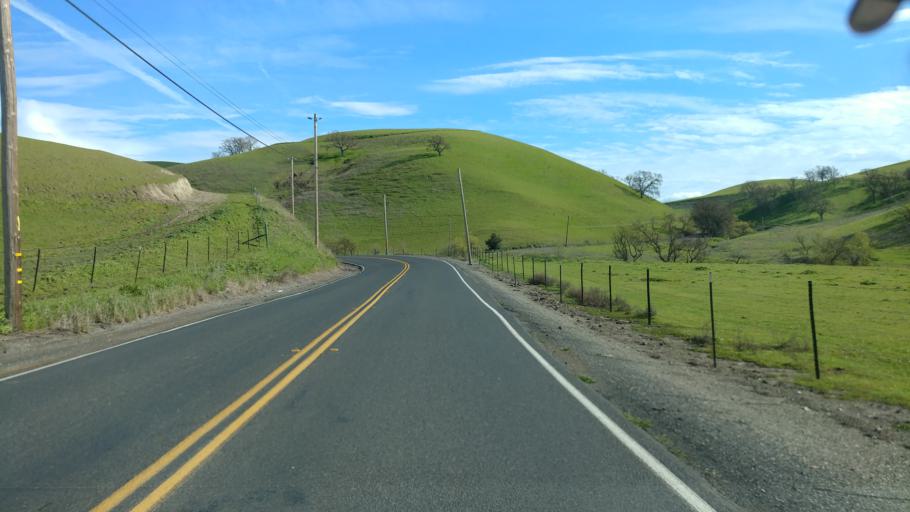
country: US
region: California
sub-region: Contra Costa County
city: Blackhawk
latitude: 37.7772
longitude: -121.8307
